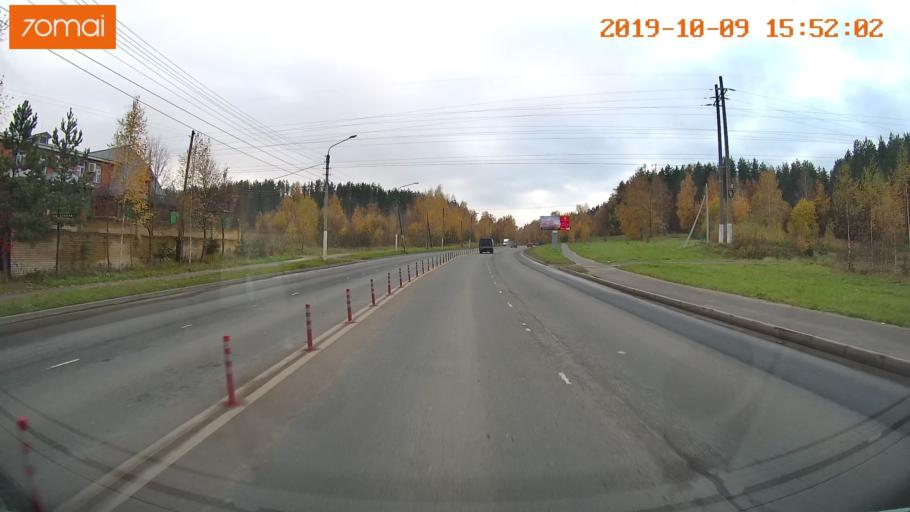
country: RU
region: Kostroma
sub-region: Kostromskoy Rayon
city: Kostroma
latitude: 57.7927
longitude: 40.9730
